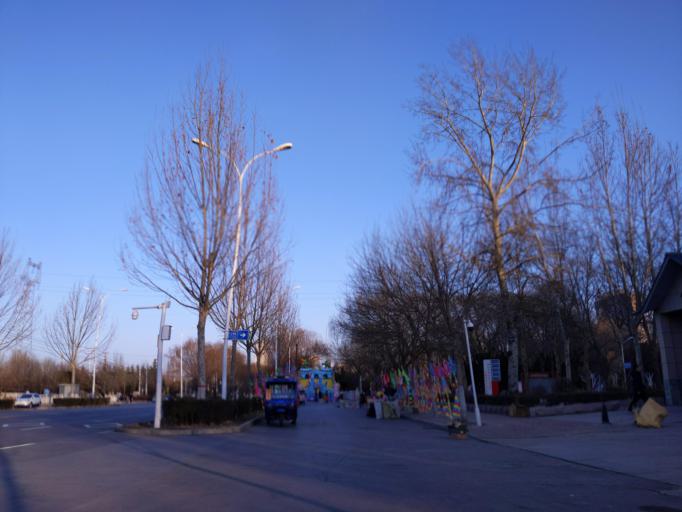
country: CN
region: Henan Sheng
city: Puyang
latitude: 35.7659
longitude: 115.0004
